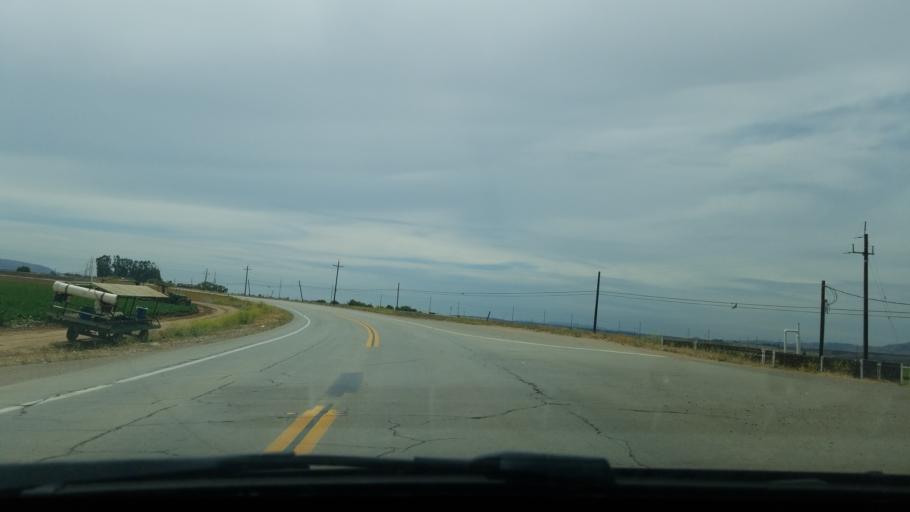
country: US
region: California
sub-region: Santa Barbara County
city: Santa Maria
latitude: 34.9228
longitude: -120.3499
